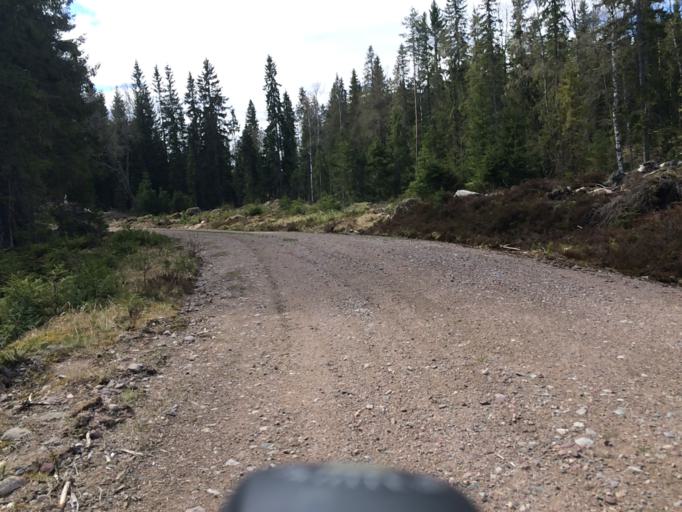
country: SE
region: OErebro
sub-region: Hallefors Kommun
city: Haellefors
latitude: 60.0481
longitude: 14.5159
